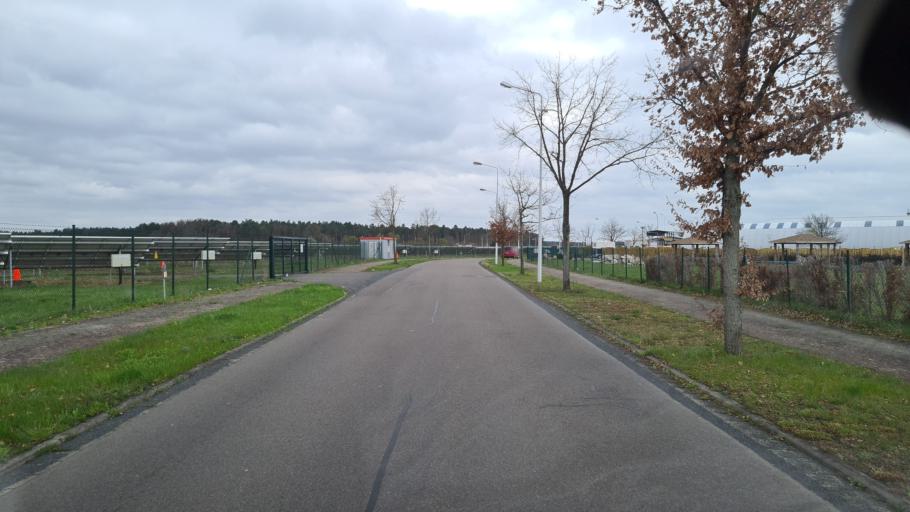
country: DE
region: Brandenburg
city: Ruhland
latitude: 51.4573
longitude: 13.8899
